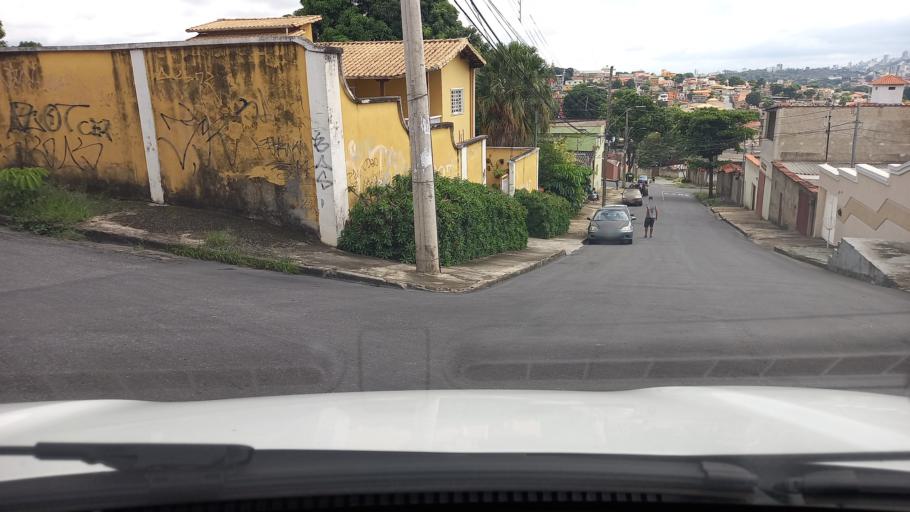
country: BR
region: Minas Gerais
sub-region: Contagem
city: Contagem
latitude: -19.8985
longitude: -44.0206
